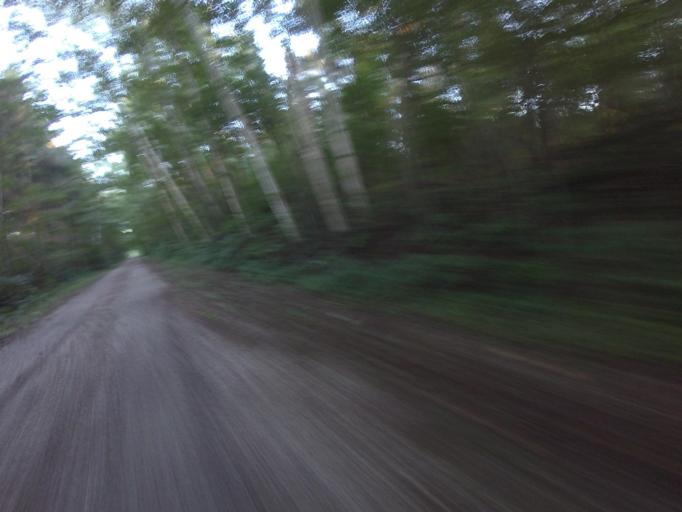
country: CA
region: Ontario
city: Goderich
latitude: 43.7529
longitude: -81.6670
